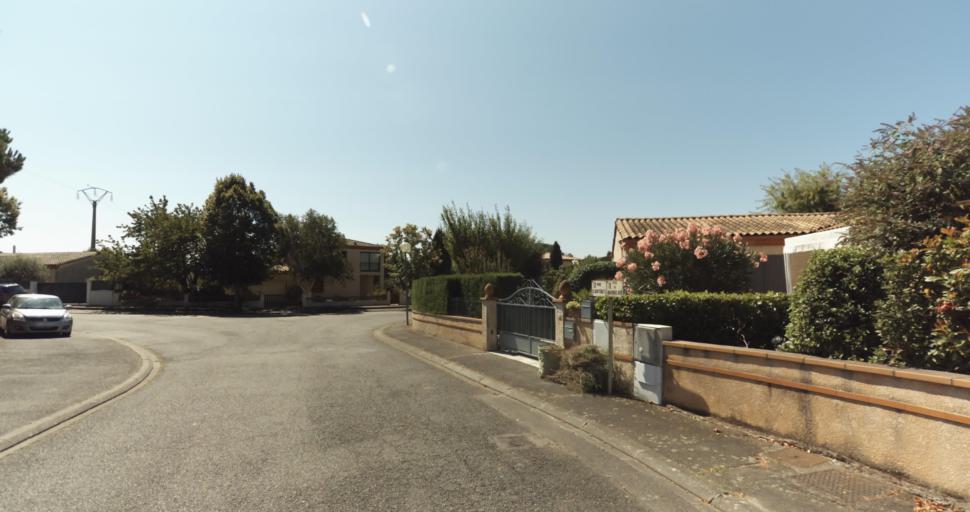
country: FR
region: Midi-Pyrenees
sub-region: Departement de la Haute-Garonne
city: L'Union
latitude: 43.6497
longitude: 1.4920
